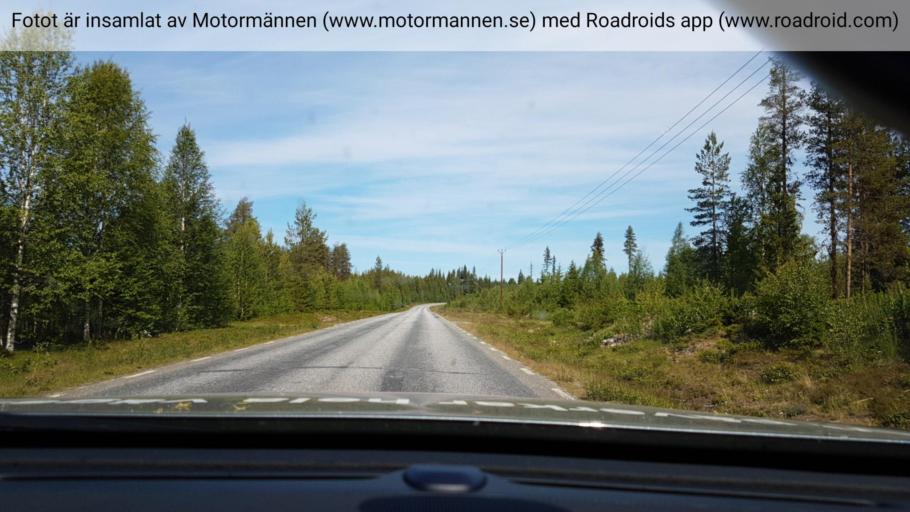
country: SE
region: Vaesterbotten
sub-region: Vilhelmina Kommun
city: Sjoberg
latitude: 64.5031
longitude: 15.9285
